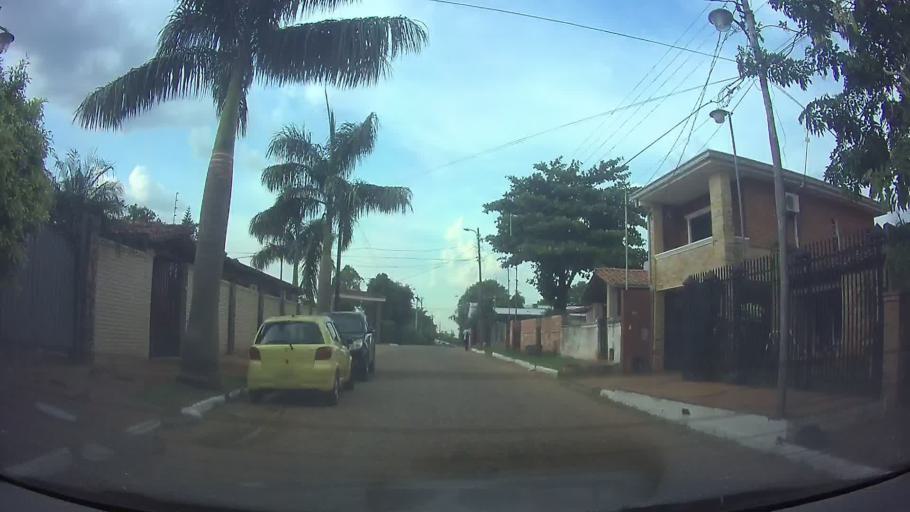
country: PY
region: Central
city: San Lorenzo
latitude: -25.2677
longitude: -57.4773
